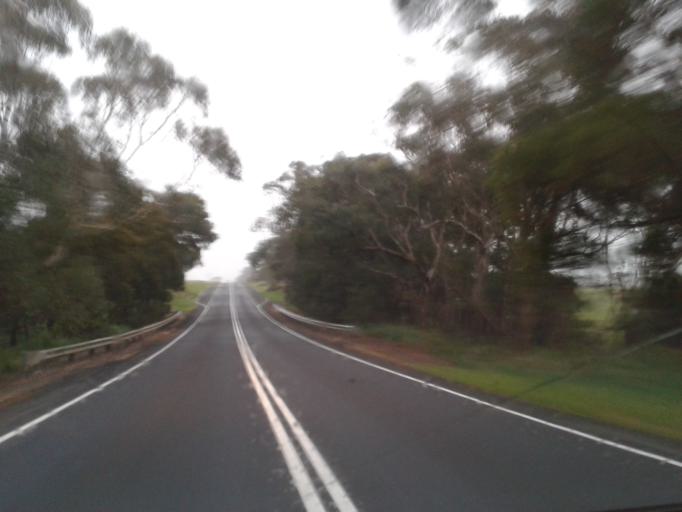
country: AU
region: Victoria
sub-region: Glenelg
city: Portland
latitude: -38.2136
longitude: 141.4213
